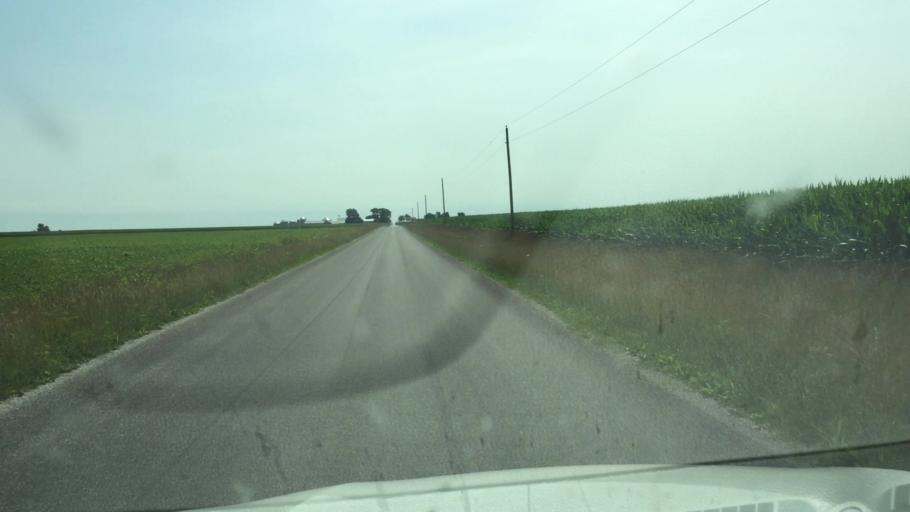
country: US
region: Illinois
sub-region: Hancock County
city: Nauvoo
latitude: 40.5075
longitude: -91.3268
